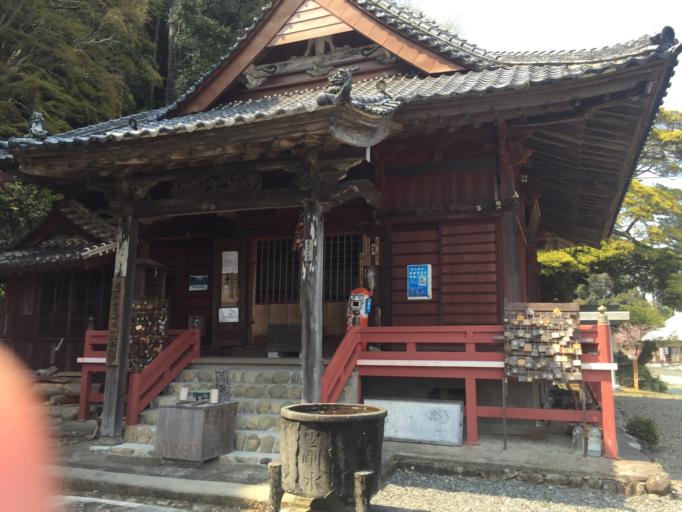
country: JP
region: Shizuoka
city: Kakegawa
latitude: 34.6927
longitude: 137.9859
